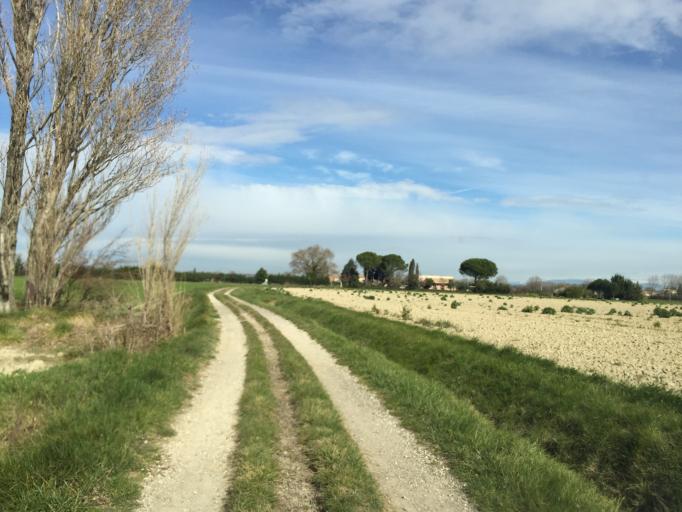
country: FR
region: Provence-Alpes-Cote d'Azur
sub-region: Departement du Vaucluse
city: Caderousse
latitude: 44.1222
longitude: 4.7510
